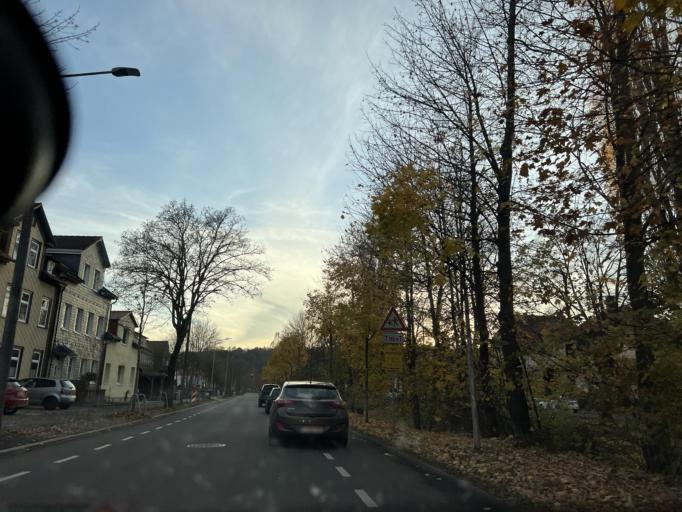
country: DE
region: Thuringia
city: Arnstadt
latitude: 50.8364
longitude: 10.9397
